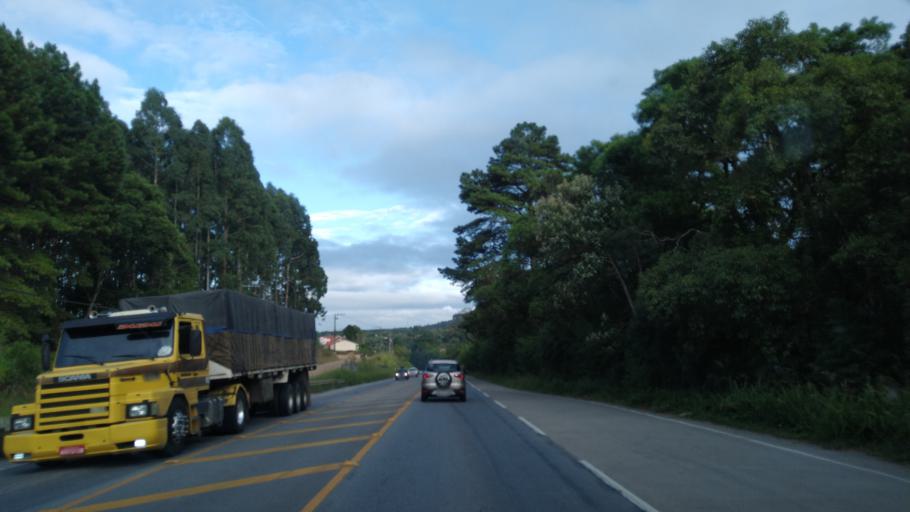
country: BR
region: Santa Catarina
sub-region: Rio Negrinho
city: Rio Negrinho
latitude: -26.2458
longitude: -49.4522
